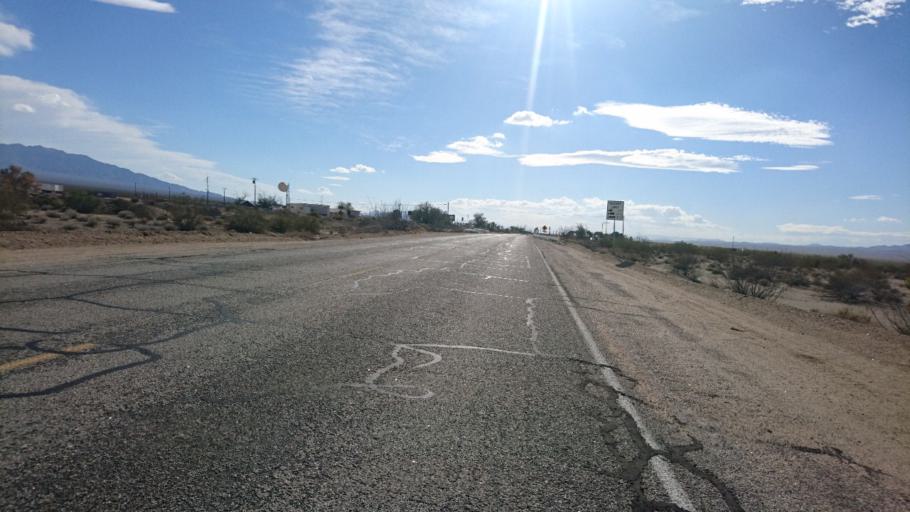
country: US
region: California
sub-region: San Bernardino County
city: Needles
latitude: 34.7370
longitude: -115.2438
